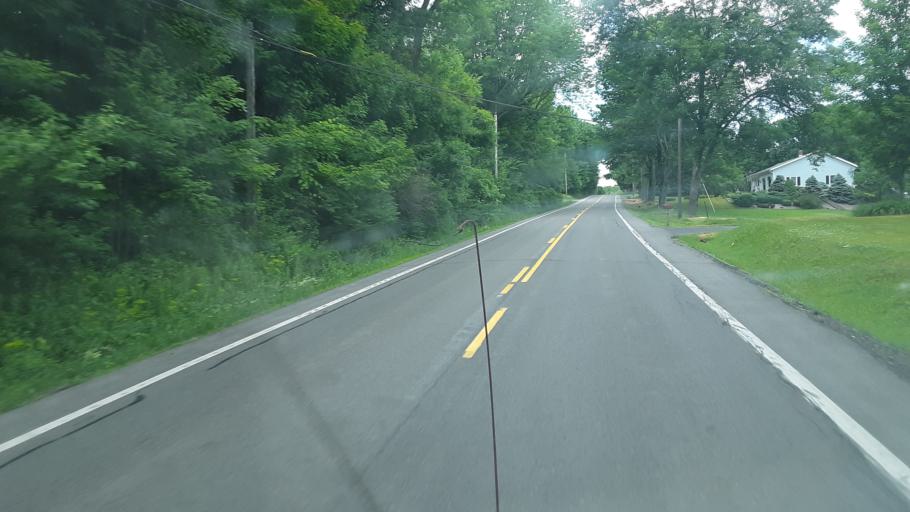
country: US
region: New York
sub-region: Oneida County
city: Rome
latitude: 43.3214
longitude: -75.4766
